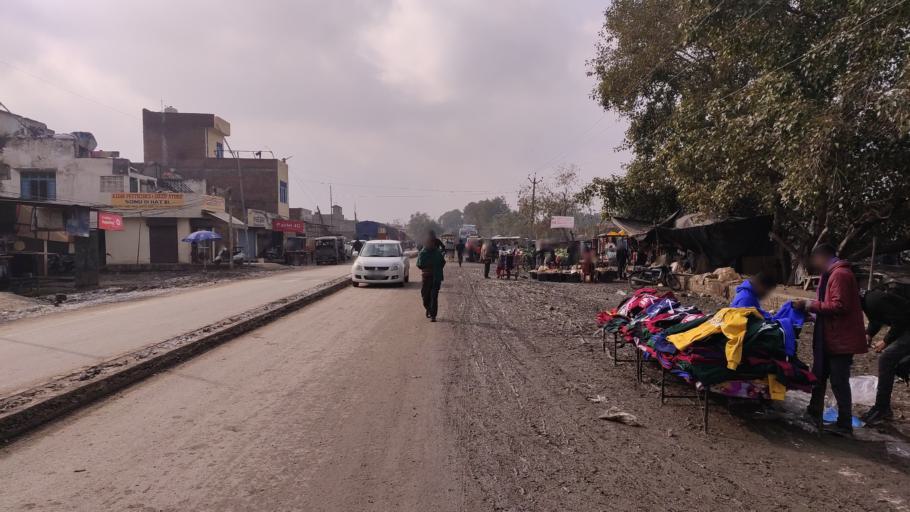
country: IN
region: Punjab
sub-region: Amritsar
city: Amritsar
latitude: 31.6258
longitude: 74.9232
